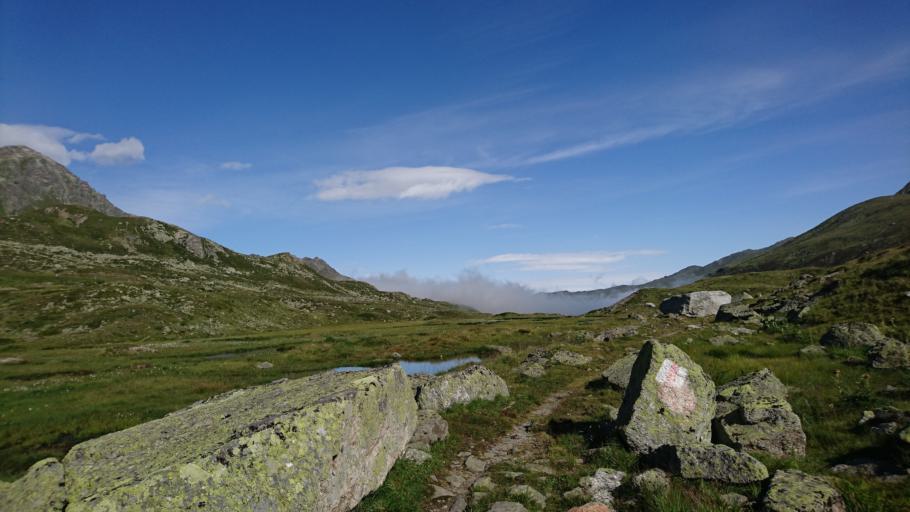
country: CH
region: Grisons
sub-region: Praettigau/Davos District
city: Davos
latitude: 46.7617
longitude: 9.9443
